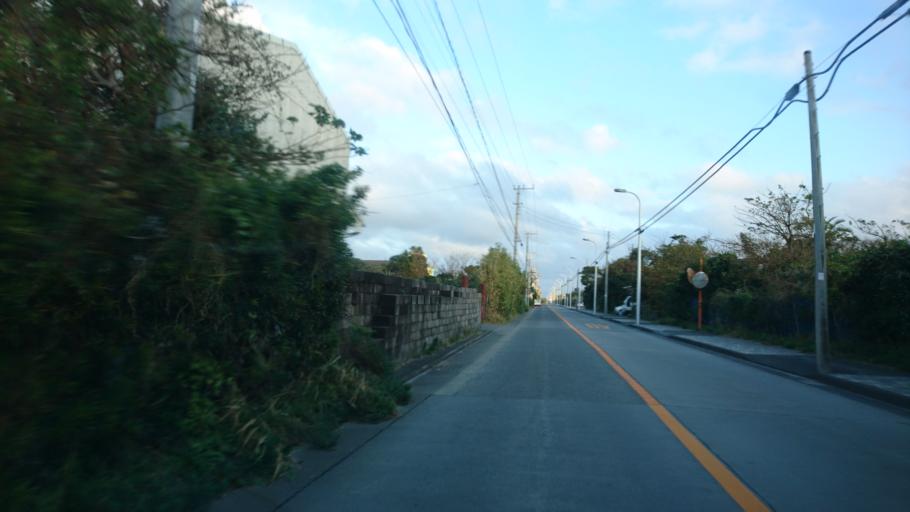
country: JP
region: Shizuoka
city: Shimoda
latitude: 34.3722
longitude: 139.2604
